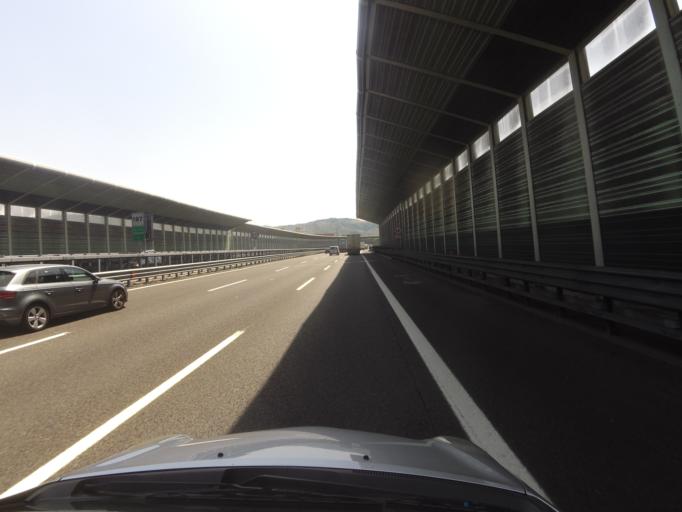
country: IT
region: Emilia-Romagna
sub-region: Provincia di Bologna
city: Casalecchio di Reno
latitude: 44.4718
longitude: 11.2718
